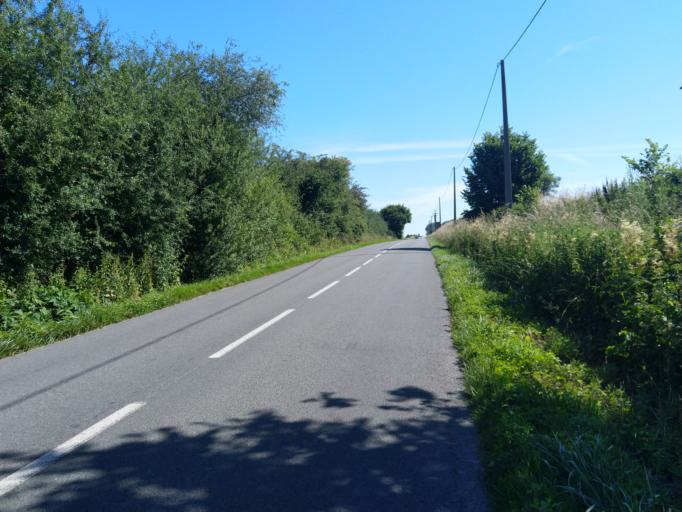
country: FR
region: Nord-Pas-de-Calais
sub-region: Departement du Nord
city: Bavay
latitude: 50.3077
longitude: 3.8034
